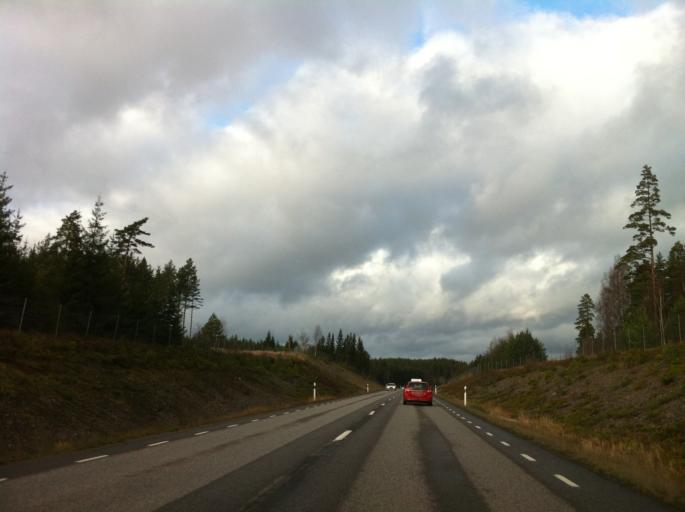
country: SE
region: Kalmar
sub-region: Vimmerby Kommun
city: Vimmerby
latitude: 57.6015
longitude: 15.8457
